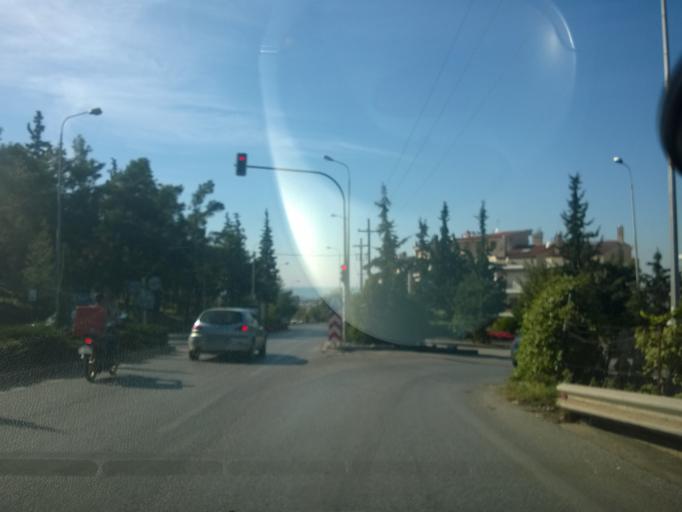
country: GR
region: Central Macedonia
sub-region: Nomos Thessalonikis
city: Pylaia
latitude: 40.5999
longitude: 22.9953
